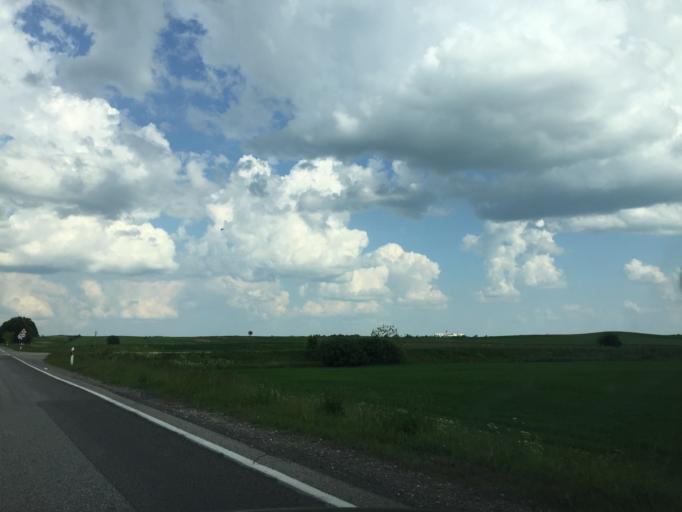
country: LT
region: Klaipedos apskritis
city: Kretinga
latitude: 55.8966
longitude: 21.1743
